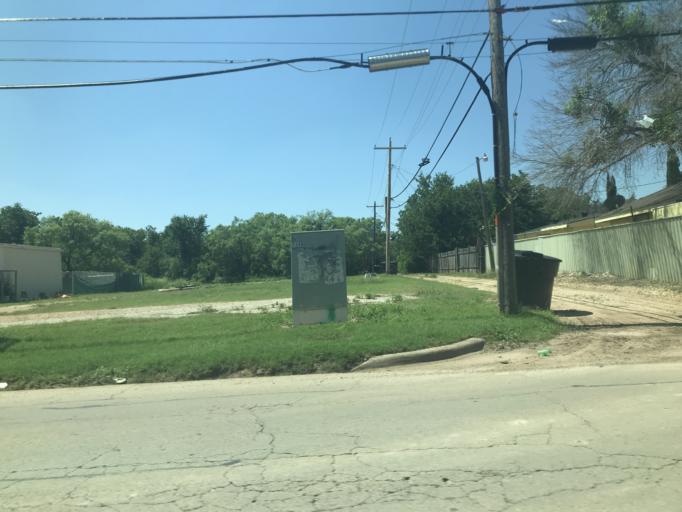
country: US
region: Texas
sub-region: Taylor County
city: Abilene
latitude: 32.4632
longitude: -99.7528
